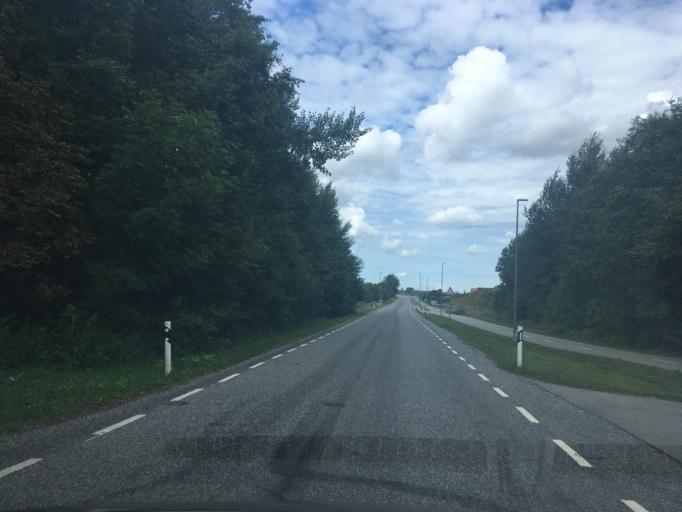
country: EE
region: Harju
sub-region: Rae vald
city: Jueri
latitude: 59.3855
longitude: 24.8584
